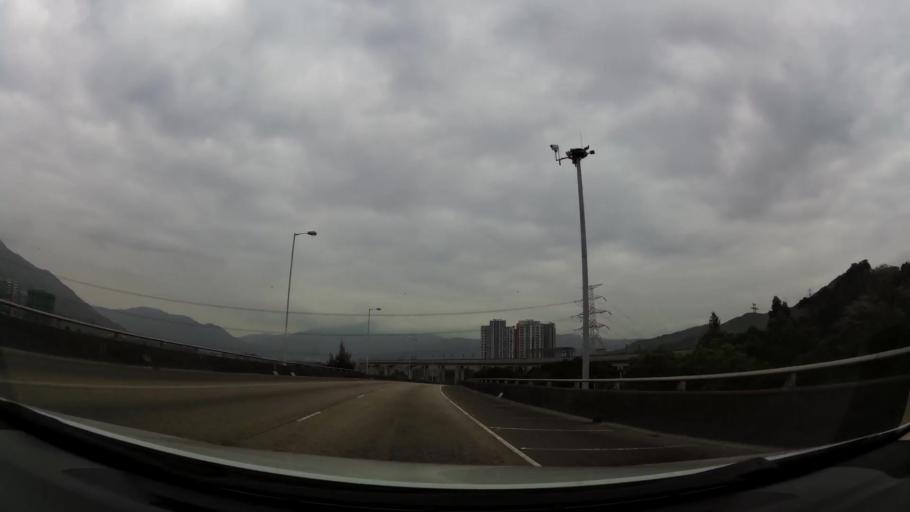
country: HK
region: Yuen Long
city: Yuen Long Kau Hui
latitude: 22.4484
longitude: 114.0485
